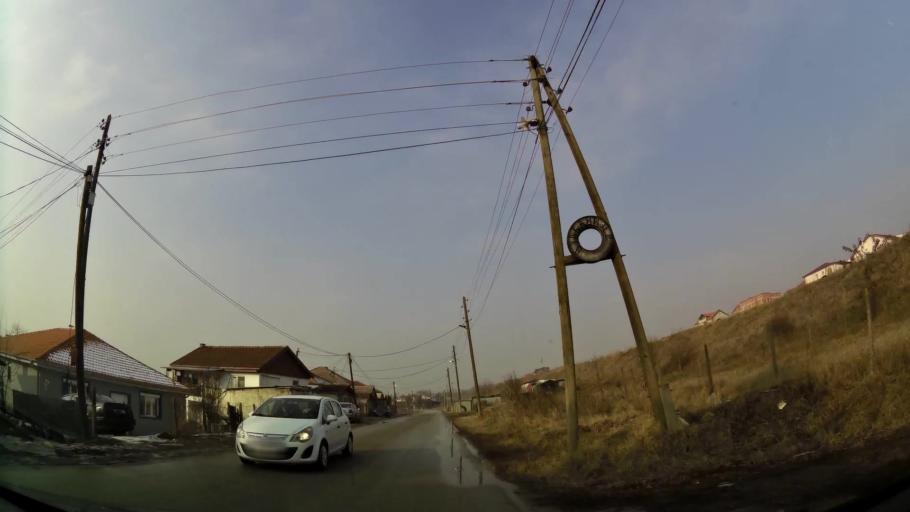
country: MK
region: Ilinden
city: Marino
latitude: 41.9844
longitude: 21.5948
